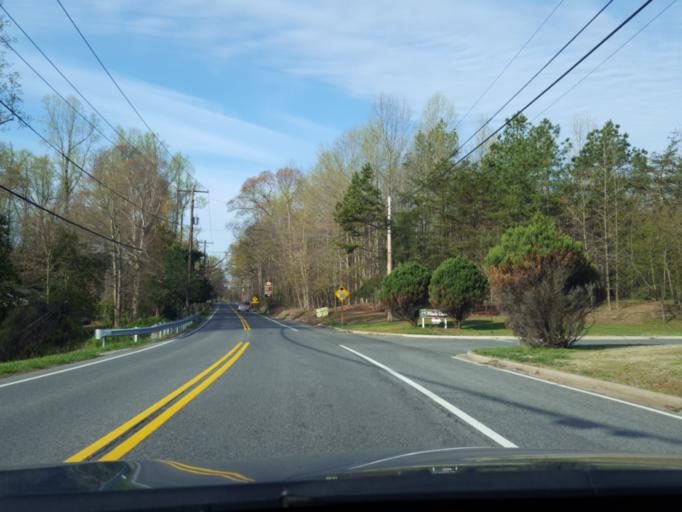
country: US
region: Maryland
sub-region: Prince George's County
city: Croom
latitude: 38.7630
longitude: -76.7567
